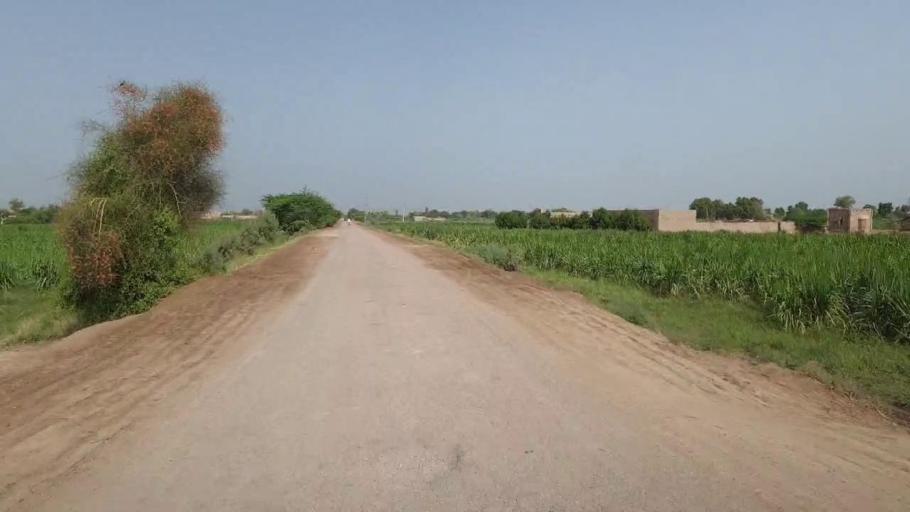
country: PK
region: Sindh
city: Daulatpur
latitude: 26.5480
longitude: 68.0621
